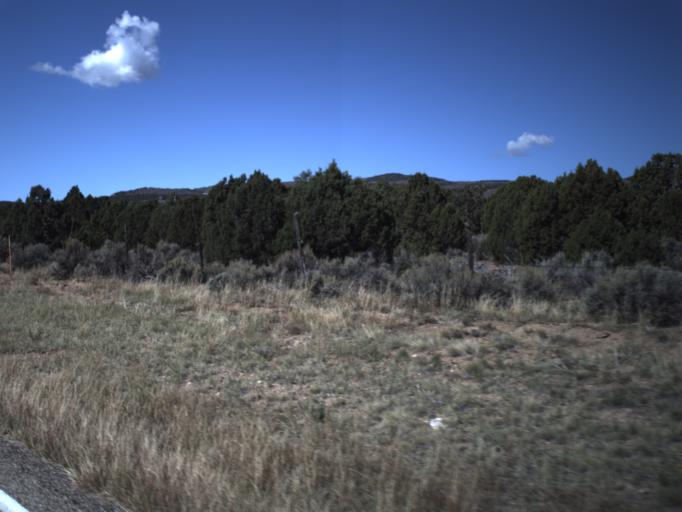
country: US
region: Utah
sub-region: Iron County
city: Cedar City
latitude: 37.6443
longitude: -113.2469
